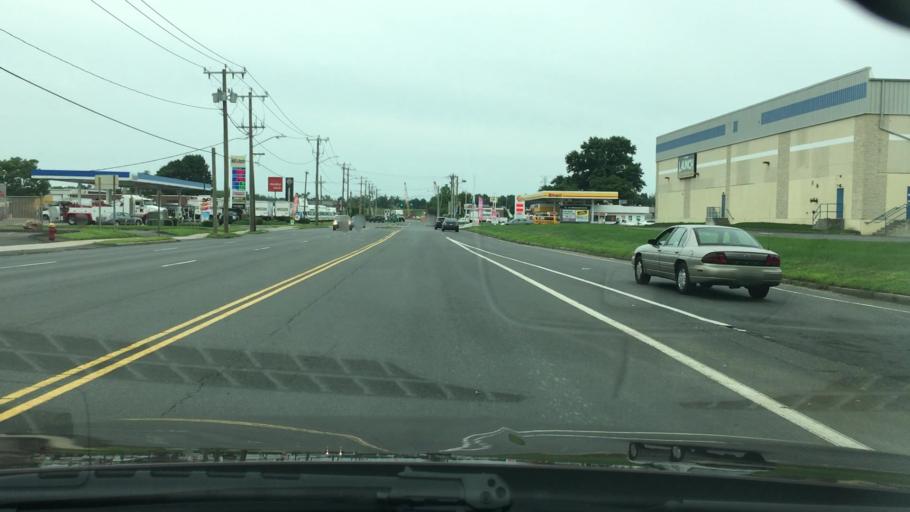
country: US
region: Connecticut
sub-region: Hartford County
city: Wethersfield
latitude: 41.7384
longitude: -72.6600
